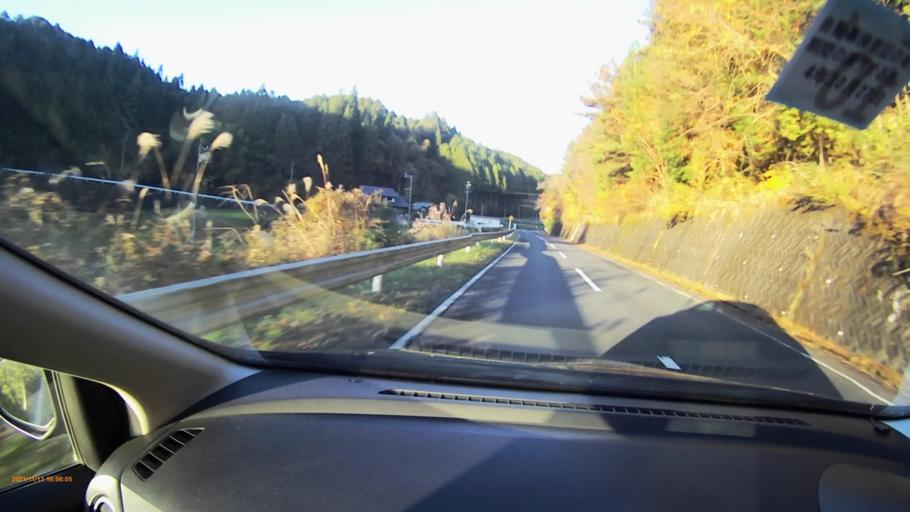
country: JP
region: Gifu
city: Nakatsugawa
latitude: 35.6029
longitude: 137.4750
